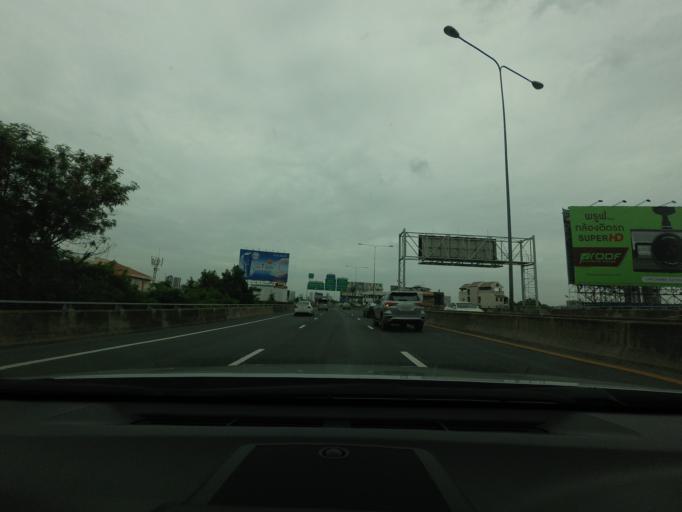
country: TH
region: Bangkok
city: Sathon
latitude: 13.6997
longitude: 100.5203
